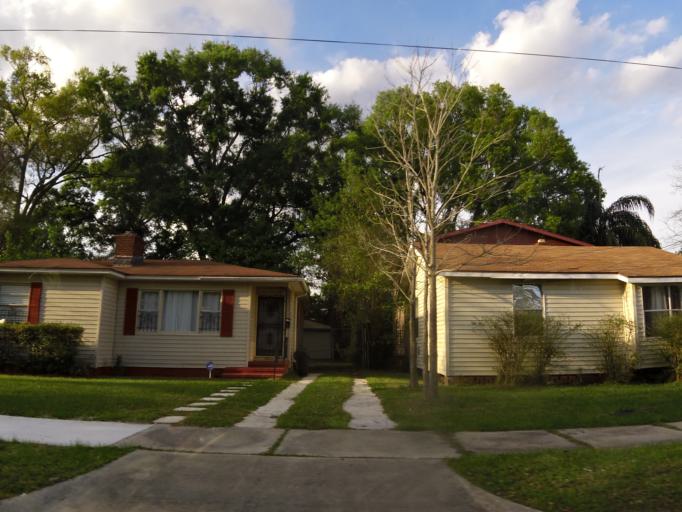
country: US
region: Florida
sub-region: Duval County
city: Jacksonville
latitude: 30.3482
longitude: -81.6790
